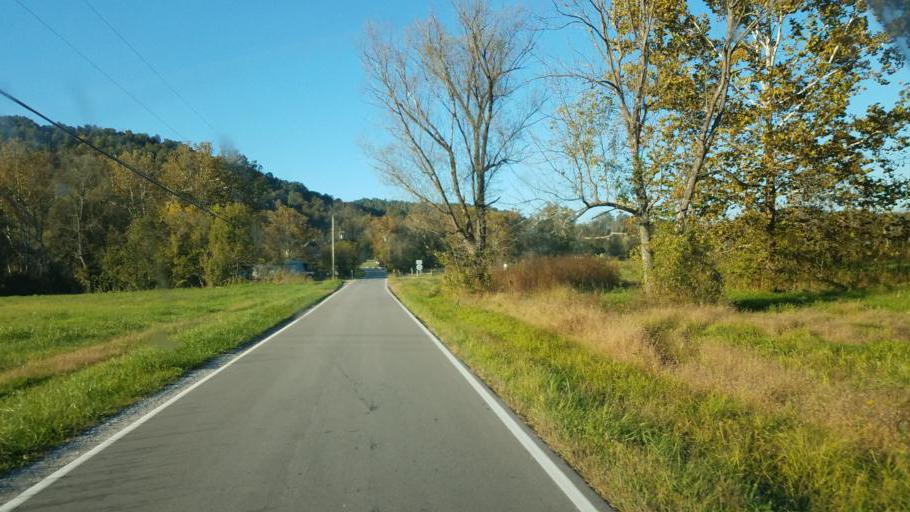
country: US
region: Kentucky
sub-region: Lewis County
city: Vanceburg
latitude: 38.5693
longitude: -83.4328
